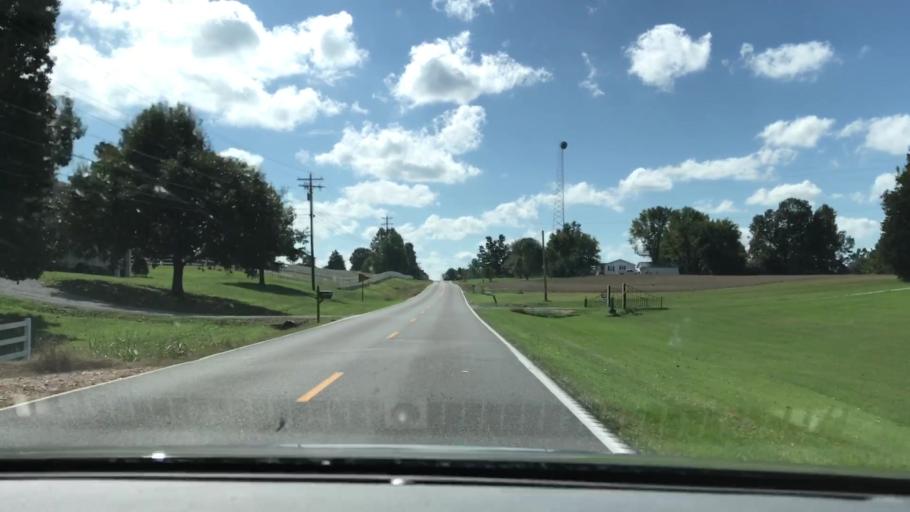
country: US
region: Kentucky
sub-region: McCracken County
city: Reidland
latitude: 36.9309
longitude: -88.5183
